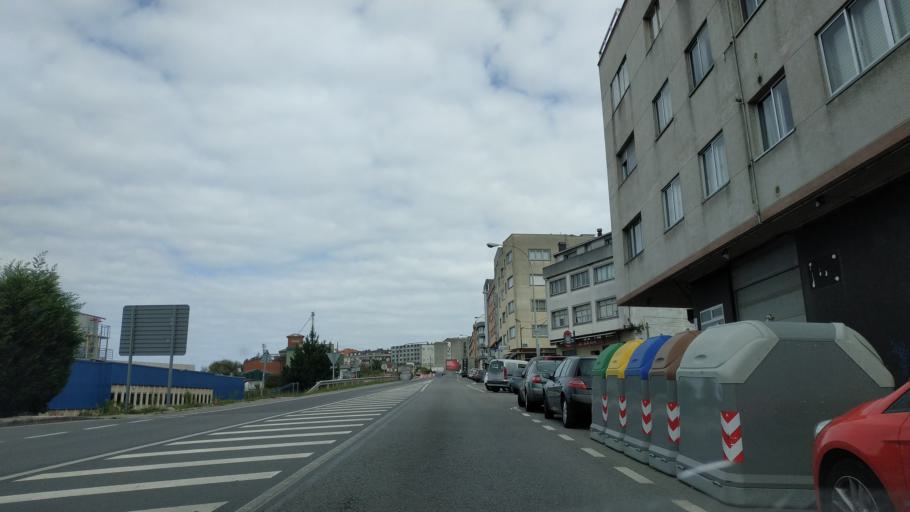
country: ES
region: Galicia
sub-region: Provincia da Coruna
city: Arteixo
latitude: 43.3088
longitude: -8.5039
